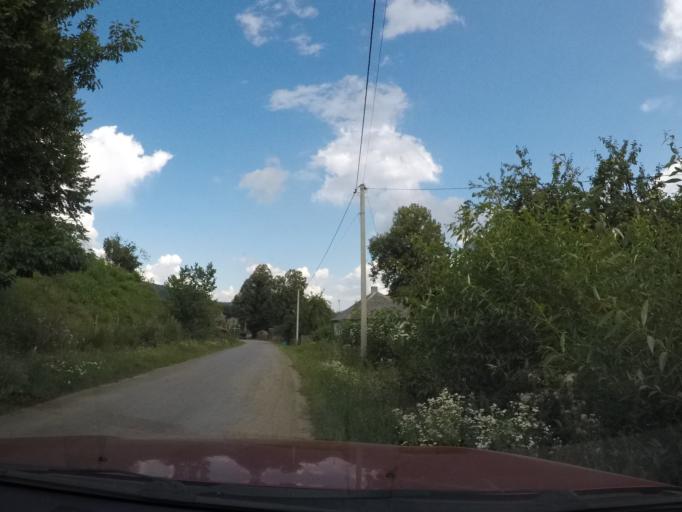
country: UA
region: Zakarpattia
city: Velykyi Bereznyi
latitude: 49.0243
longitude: 22.6075
